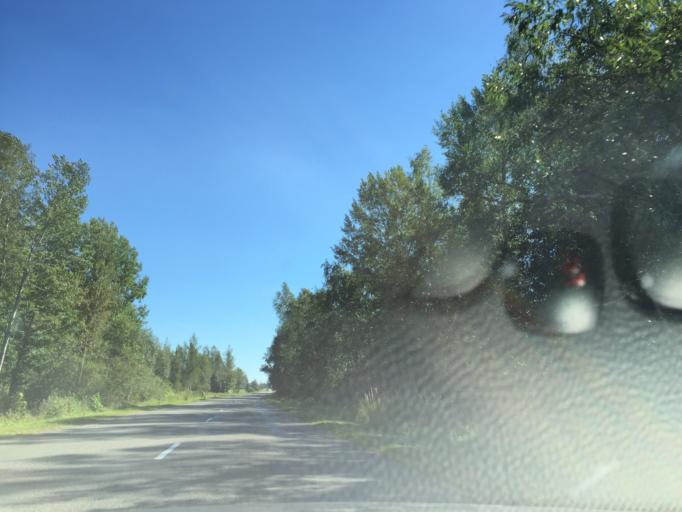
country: LV
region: Akniste
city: Akniste
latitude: 56.0715
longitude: 25.8894
